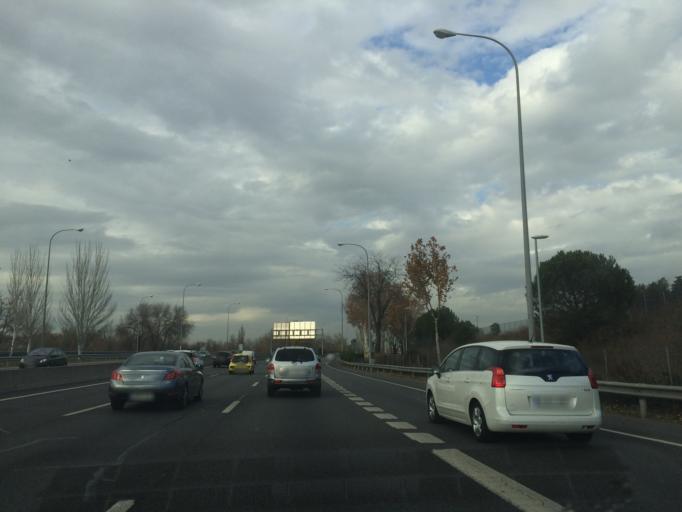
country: ES
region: Madrid
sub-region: Provincia de Madrid
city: Moncloa-Aravaca
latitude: 40.4391
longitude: -3.7382
